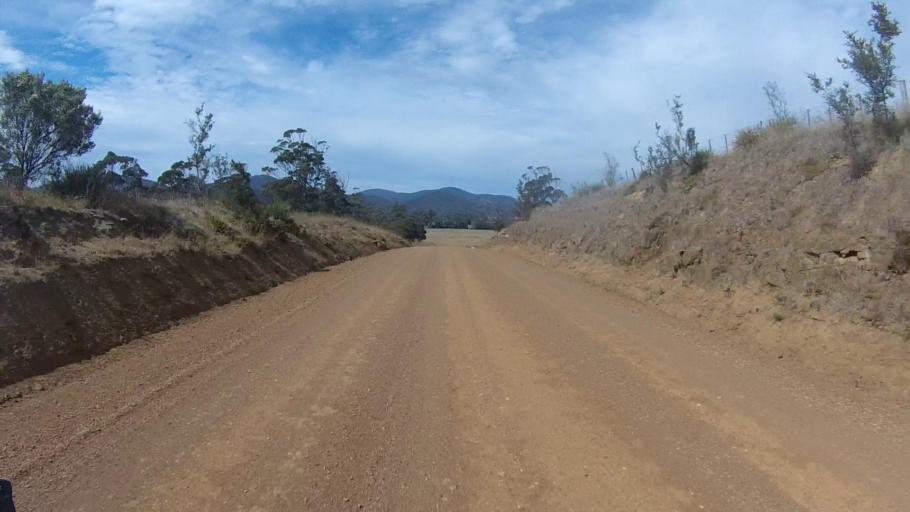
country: AU
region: Tasmania
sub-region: Sorell
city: Sorell
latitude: -42.6333
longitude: 147.9010
